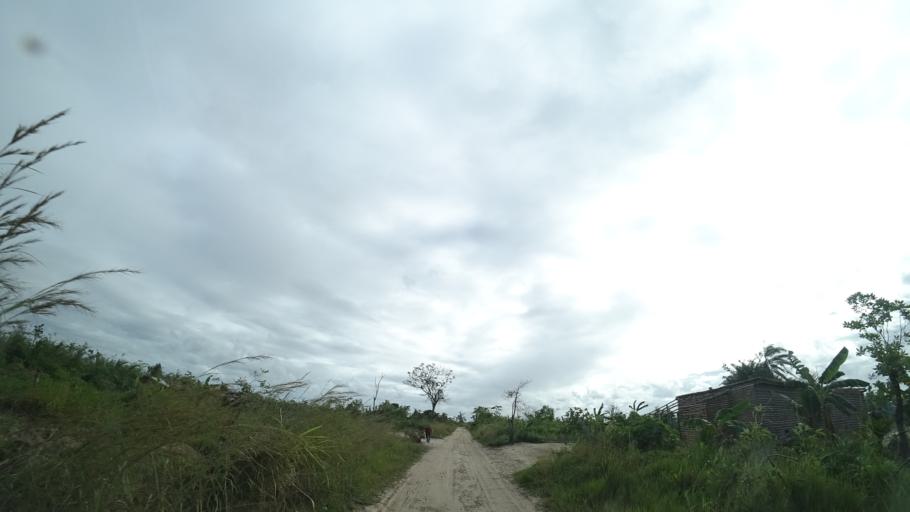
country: MZ
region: Sofala
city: Dondo
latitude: -19.5742
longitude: 35.1026
